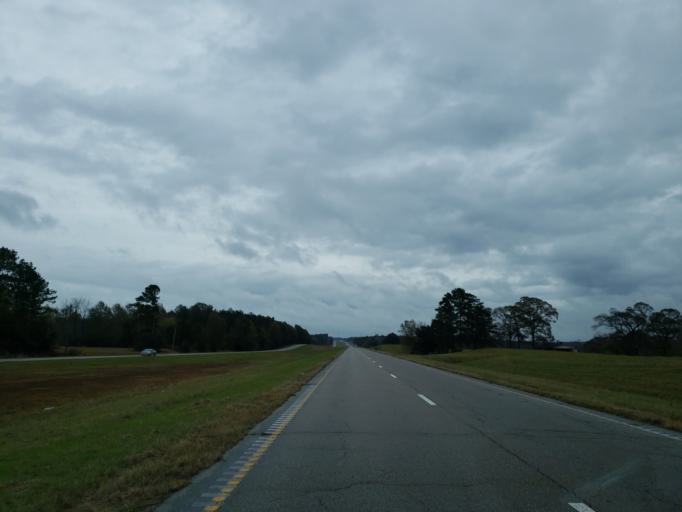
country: US
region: Mississippi
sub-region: Wayne County
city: Waynesboro
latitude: 31.6965
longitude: -88.8595
